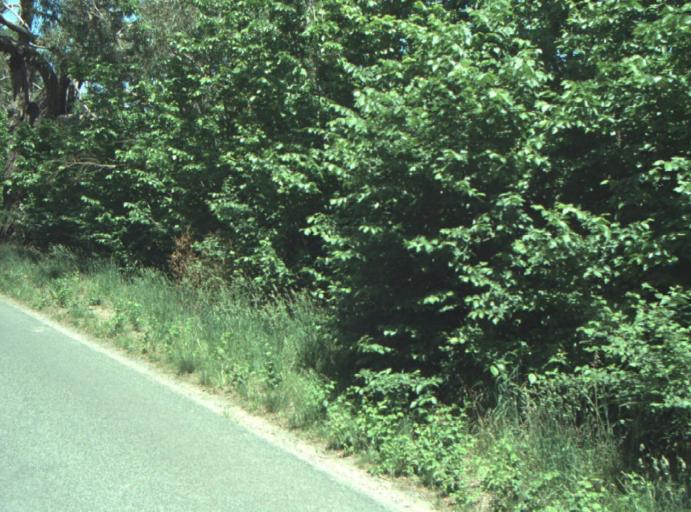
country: AU
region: Victoria
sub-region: Moorabool
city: Bacchus Marsh
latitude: -37.8279
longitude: 144.2894
